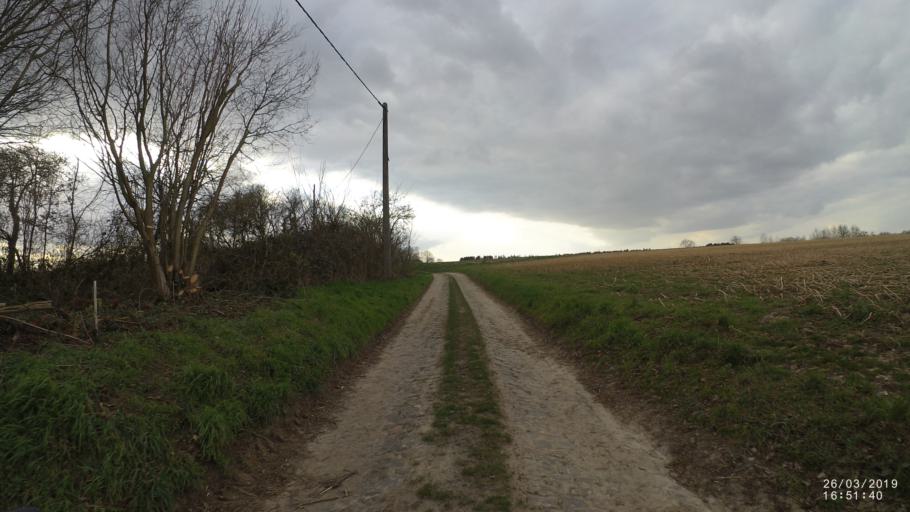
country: BE
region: Flanders
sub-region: Provincie Vlaams-Brabant
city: Bertem
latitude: 50.8398
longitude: 4.6351
